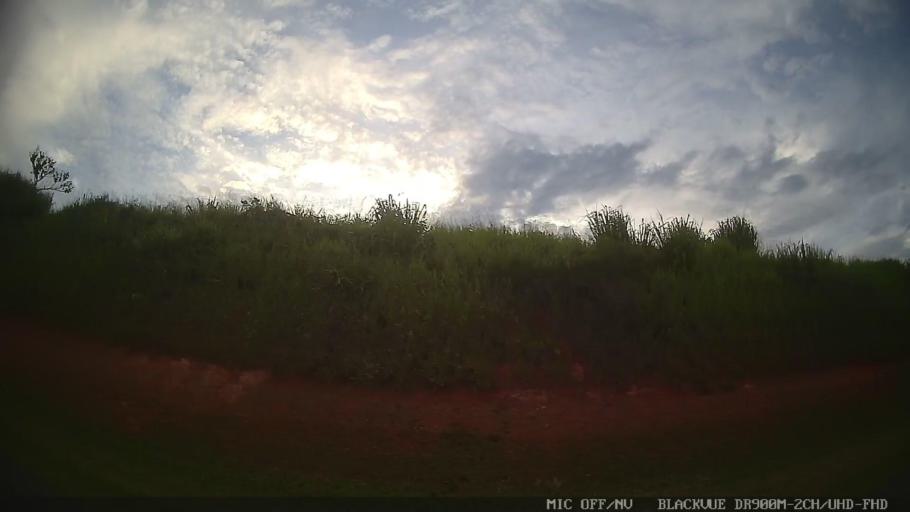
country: BR
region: Sao Paulo
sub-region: Itu
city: Itu
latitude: -23.2407
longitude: -47.2834
